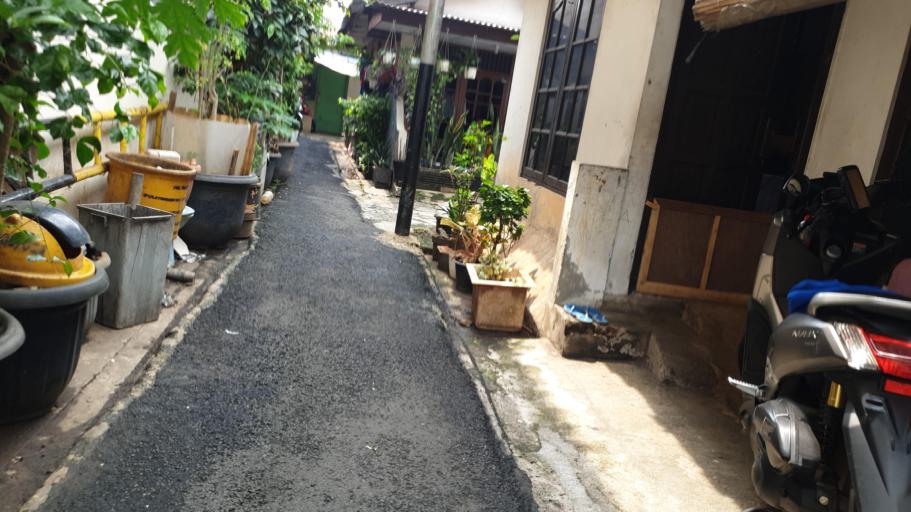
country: ID
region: Banten
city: South Tangerang
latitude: -6.2586
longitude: 106.7834
